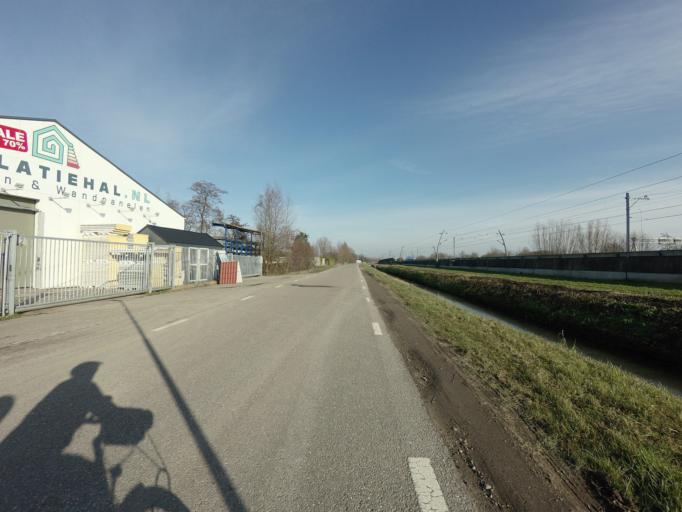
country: NL
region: South Holland
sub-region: Gemeente Giessenlanden
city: Giessenburg
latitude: 51.8387
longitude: 4.9069
